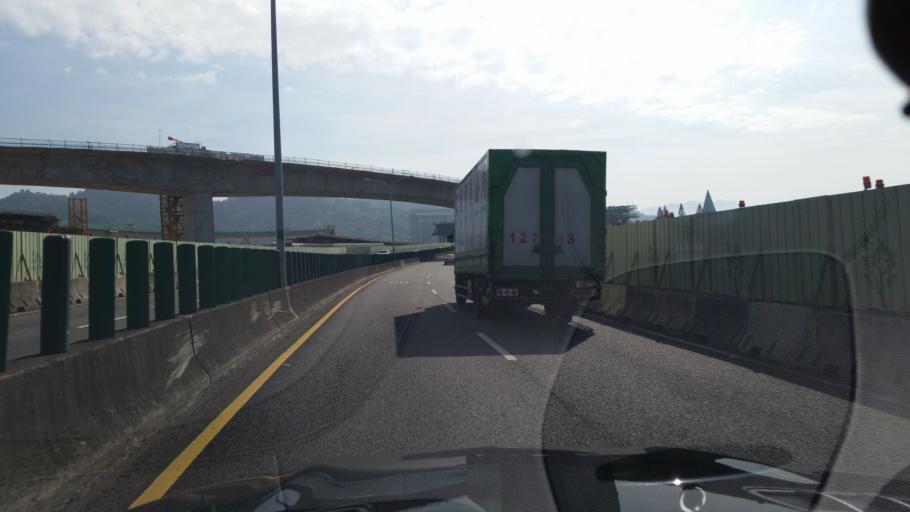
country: TW
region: Taiwan
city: Fengyuan
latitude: 24.2001
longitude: 120.7146
